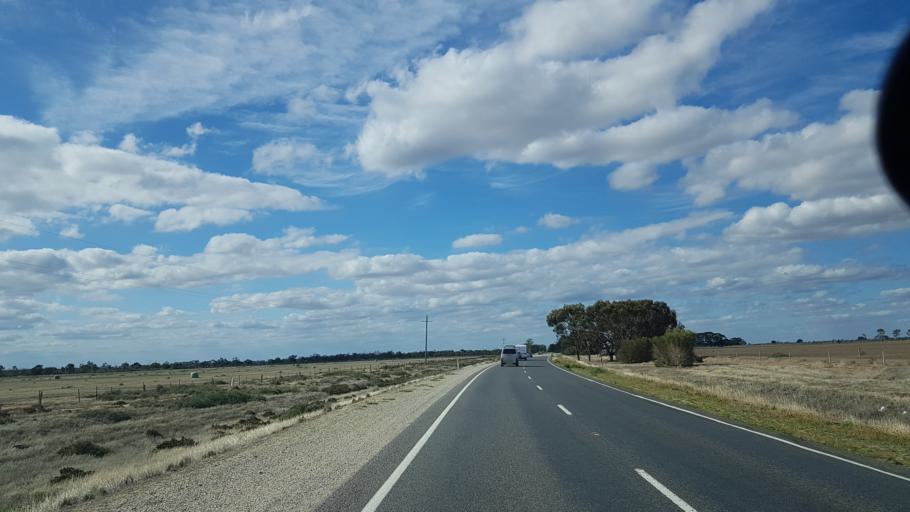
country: AU
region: Victoria
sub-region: Swan Hill
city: Swan Hill
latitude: -35.8285
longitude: 143.9453
